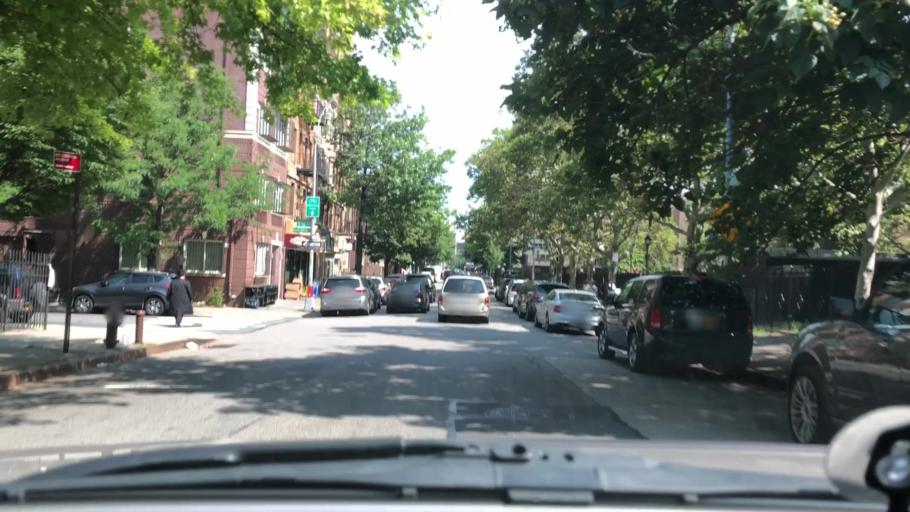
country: US
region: New York
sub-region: Queens County
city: Long Island City
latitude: 40.7078
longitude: -73.9644
